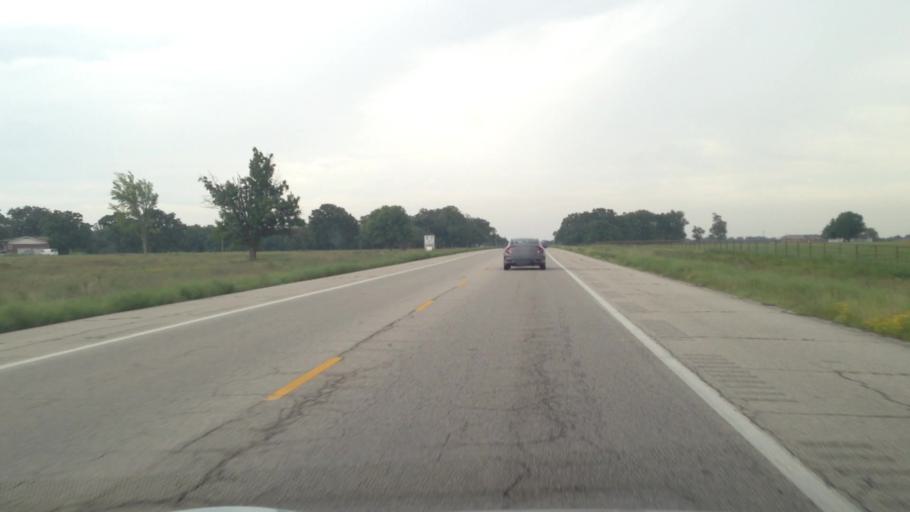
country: US
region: Kansas
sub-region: Cherokee County
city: Galena
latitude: 37.0165
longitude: -94.6349
